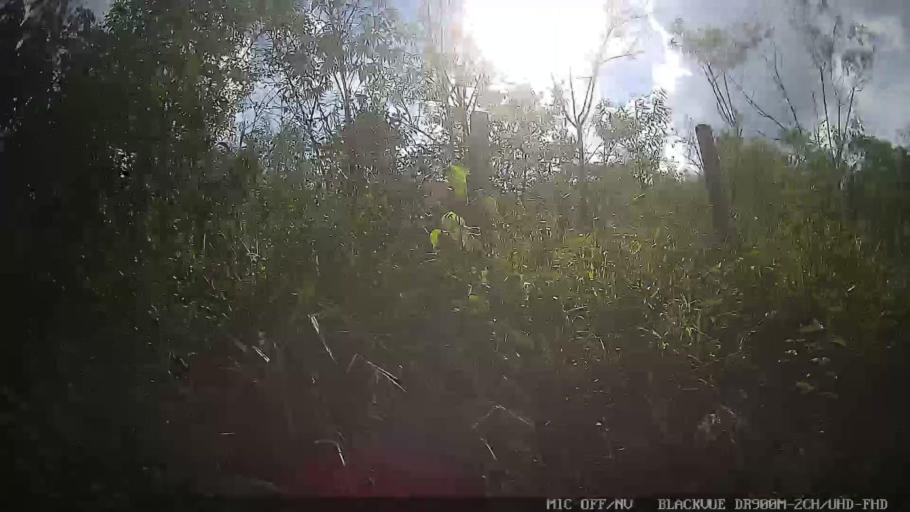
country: BR
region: Minas Gerais
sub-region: Extrema
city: Extrema
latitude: -22.8344
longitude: -46.2481
